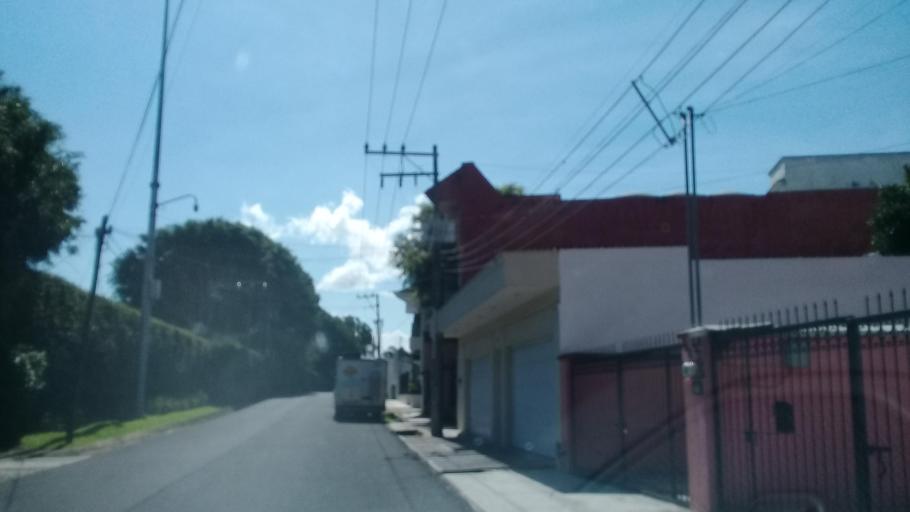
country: MX
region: Veracruz
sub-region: Tlalnelhuayocan
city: Guadalupe Victoria
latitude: 19.5277
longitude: -96.9479
